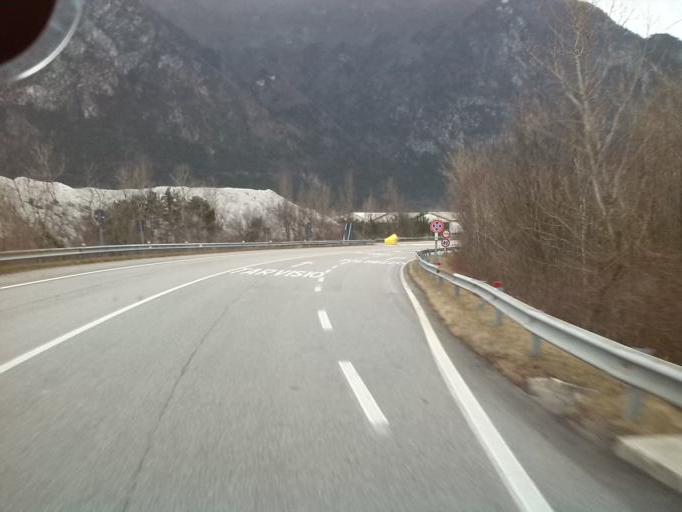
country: IT
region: Friuli Venezia Giulia
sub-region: Provincia di Udine
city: Amaro
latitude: 46.3800
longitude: 13.1330
